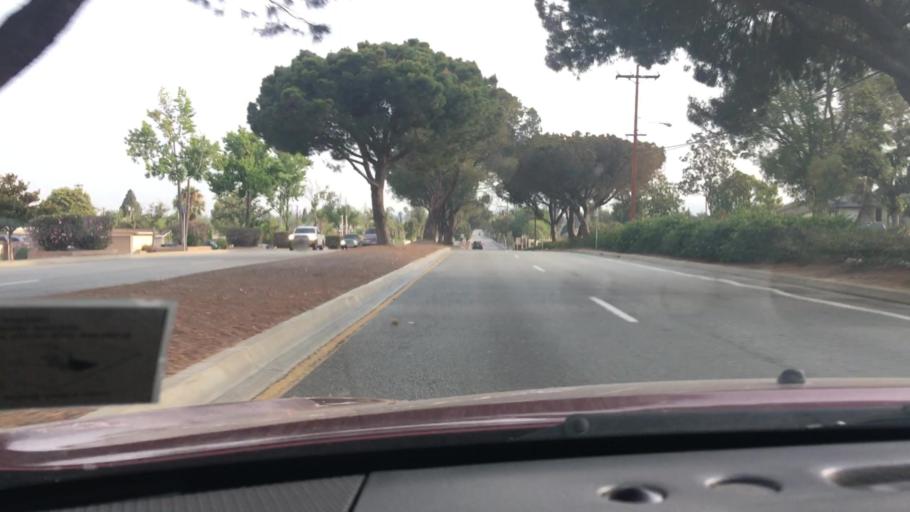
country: US
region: California
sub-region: Los Angeles County
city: La Mirada
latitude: 33.9057
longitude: -118.0292
